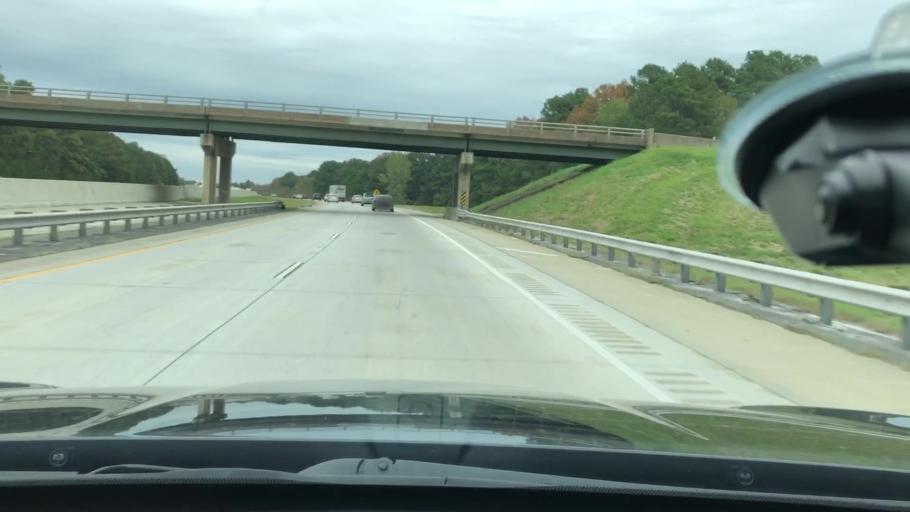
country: US
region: Arkansas
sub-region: Hempstead County
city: Hope
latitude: 33.6103
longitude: -93.7998
